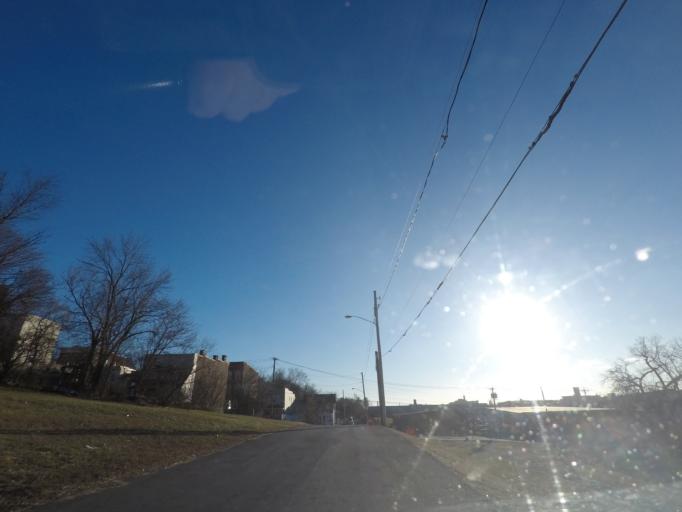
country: US
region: New York
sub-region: Albany County
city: Green Island
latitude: 42.7462
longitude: -73.6795
